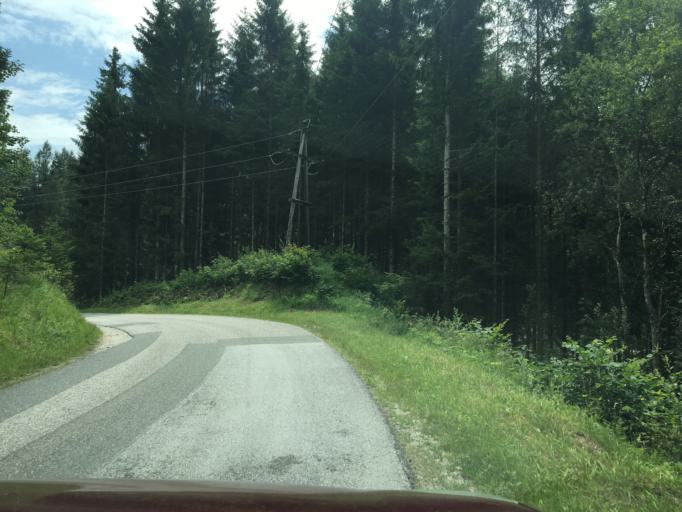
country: AT
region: Salzburg
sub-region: Politischer Bezirk Hallein
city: Scheffau am Tennengebirge
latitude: 47.6042
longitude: 13.2676
